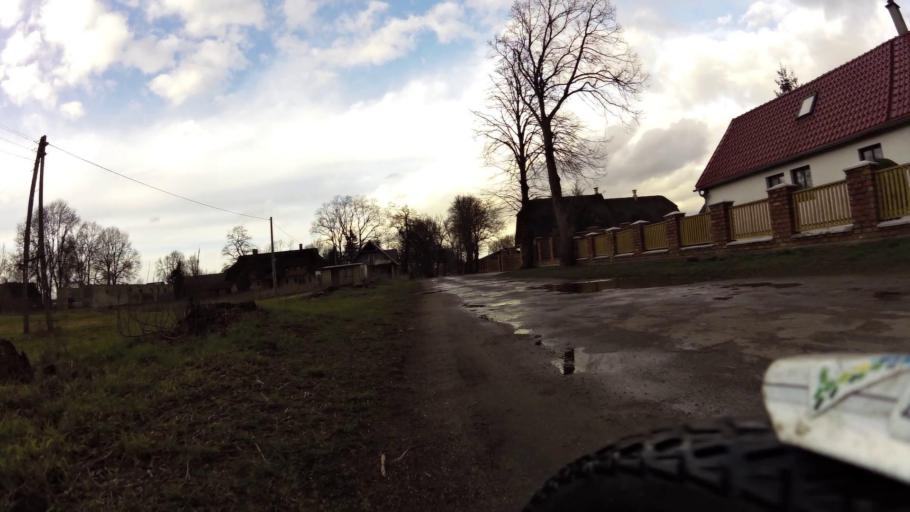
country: PL
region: West Pomeranian Voivodeship
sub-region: Powiat kamienski
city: Kamien Pomorski
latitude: 53.8955
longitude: 14.7297
